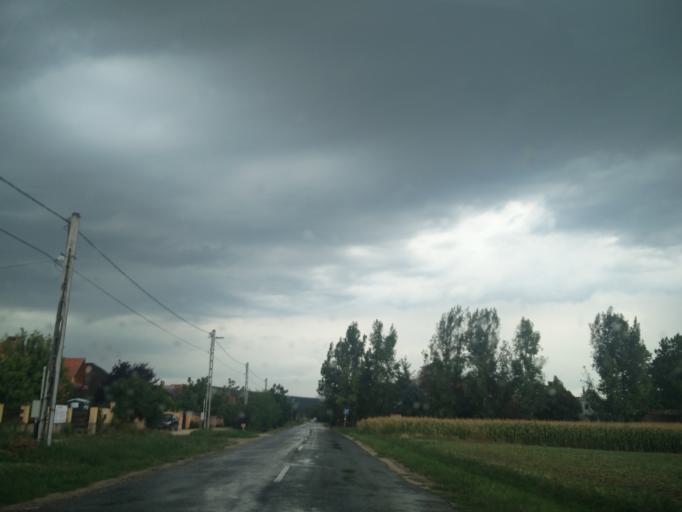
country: HU
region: Fejer
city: Velence
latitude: 47.2471
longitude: 18.6352
